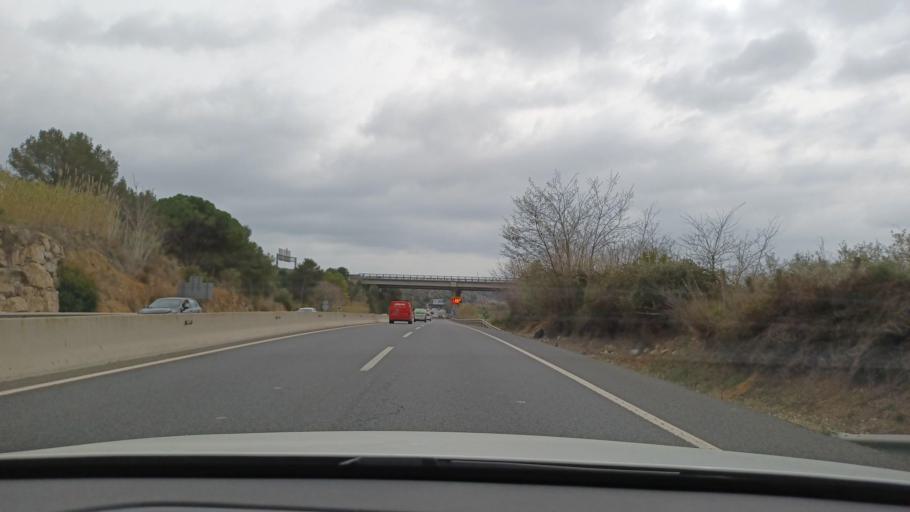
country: ES
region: Catalonia
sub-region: Provincia de Tarragona
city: Constanti
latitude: 41.1477
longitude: 1.2396
